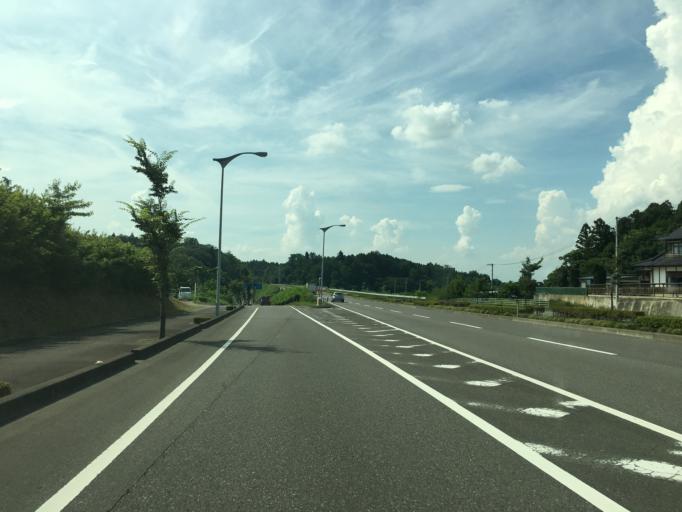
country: JP
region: Fukushima
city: Sukagawa
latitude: 37.2616
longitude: 140.4181
